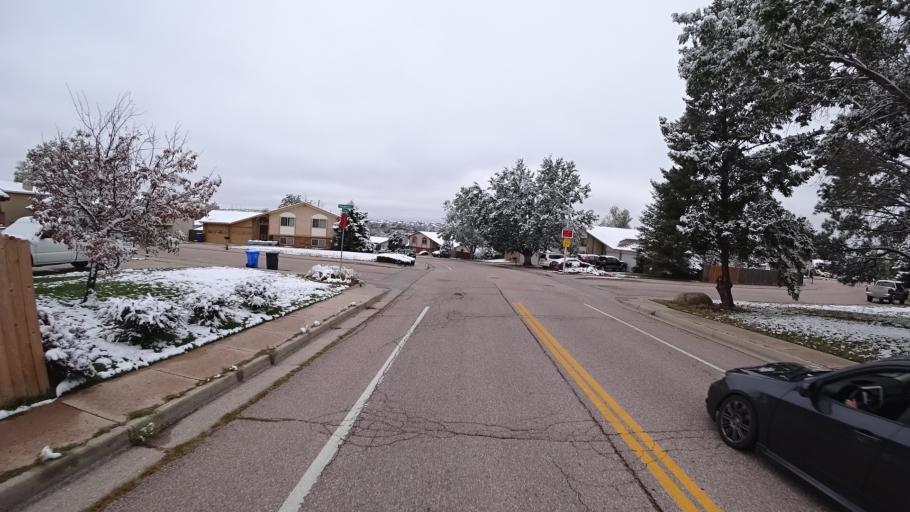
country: US
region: Colorado
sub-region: El Paso County
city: Colorado Springs
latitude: 38.9224
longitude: -104.7833
